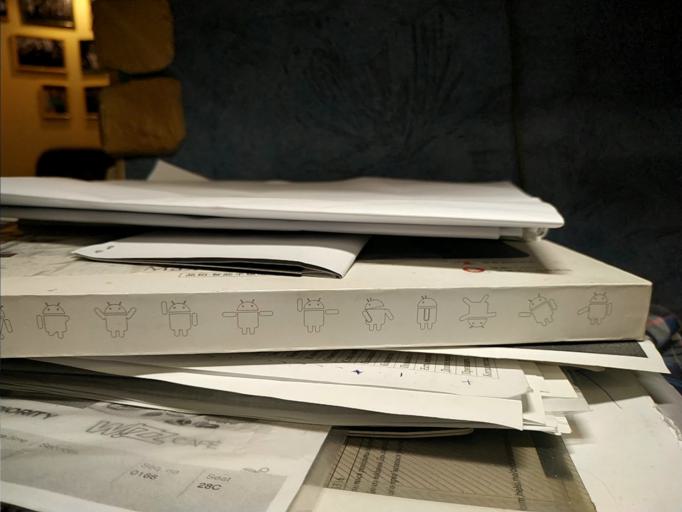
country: RU
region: Tverskaya
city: Zubtsov
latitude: 56.0796
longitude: 34.8061
